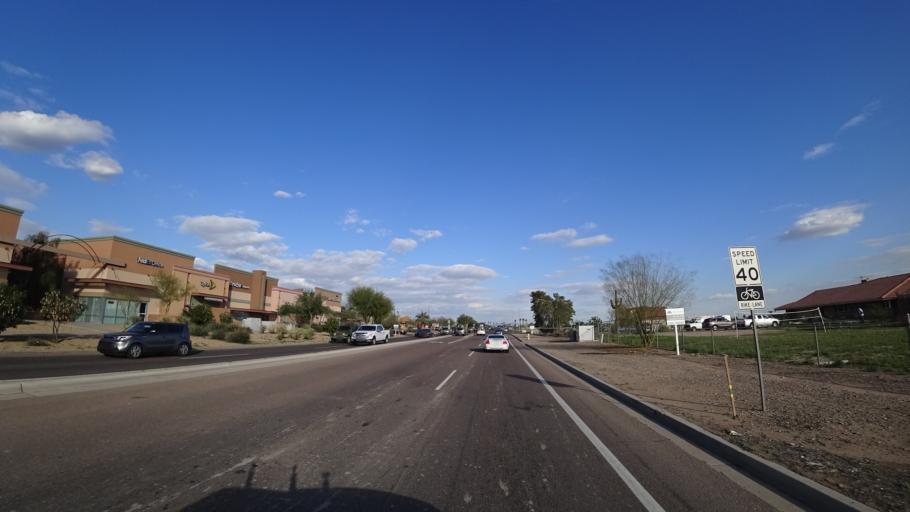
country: US
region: Arizona
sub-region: Maricopa County
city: Peoria
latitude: 33.5515
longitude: -112.2636
